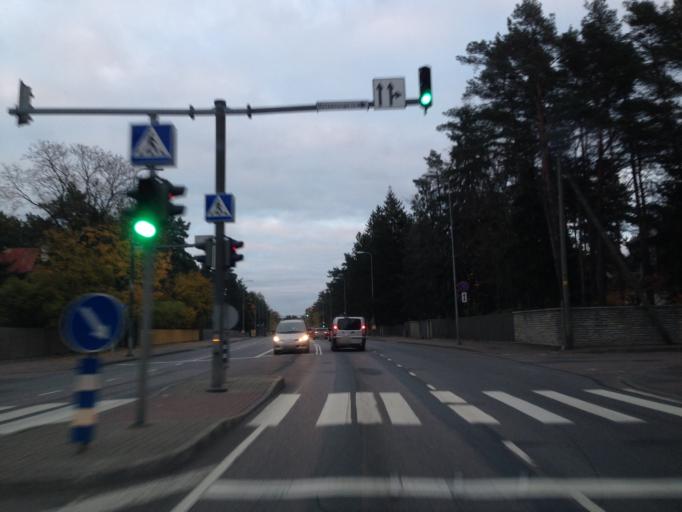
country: EE
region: Harju
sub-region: Saue vald
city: Laagri
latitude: 59.3785
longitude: 24.6908
